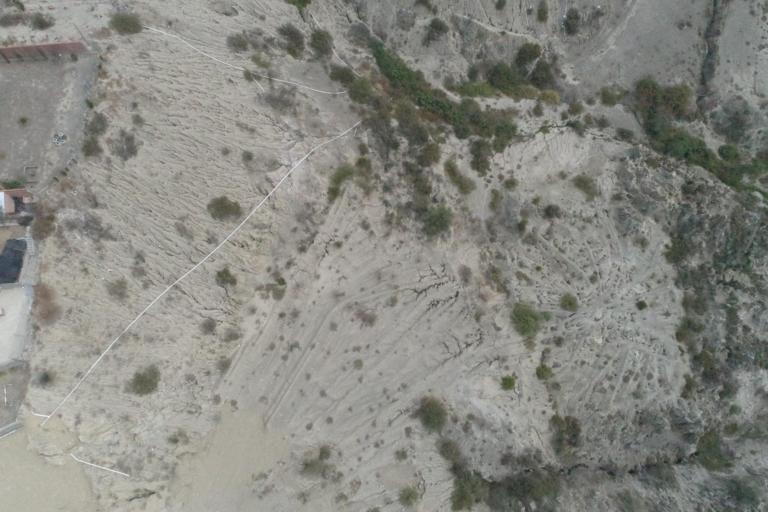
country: BO
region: La Paz
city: La Paz
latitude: -16.6002
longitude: -68.0678
